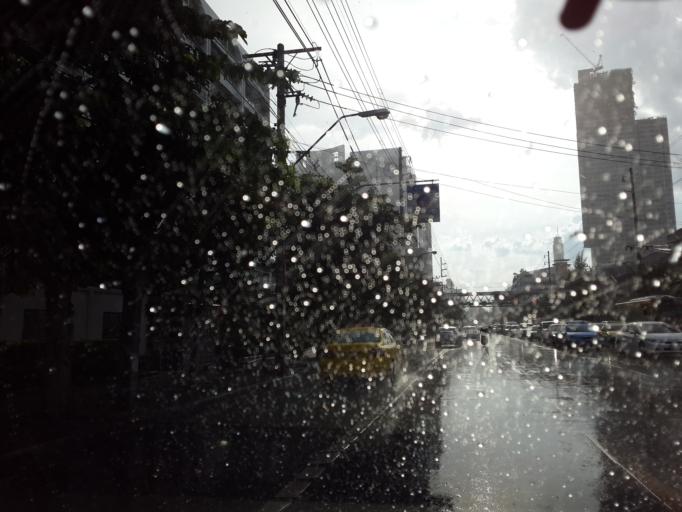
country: TH
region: Bangkok
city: Din Daeng
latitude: 13.7492
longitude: 100.5607
